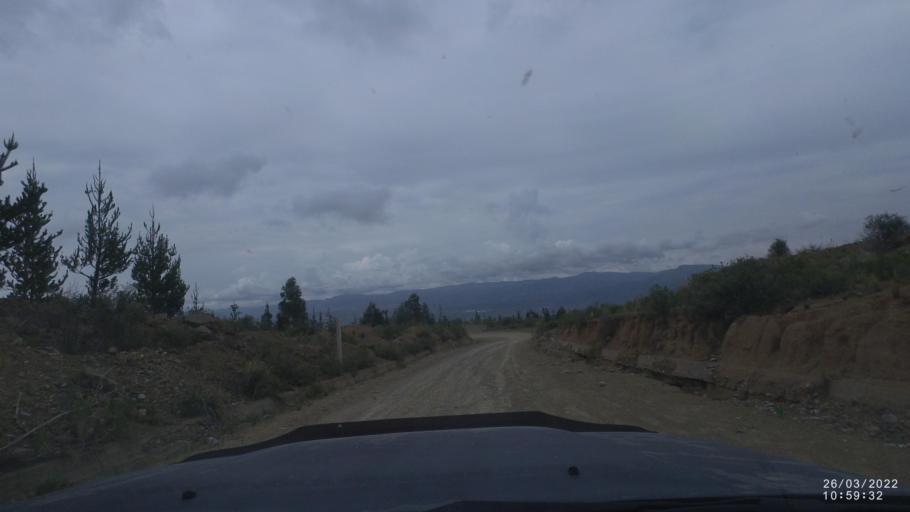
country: BO
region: Cochabamba
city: Tarata
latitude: -17.5143
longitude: -66.0253
